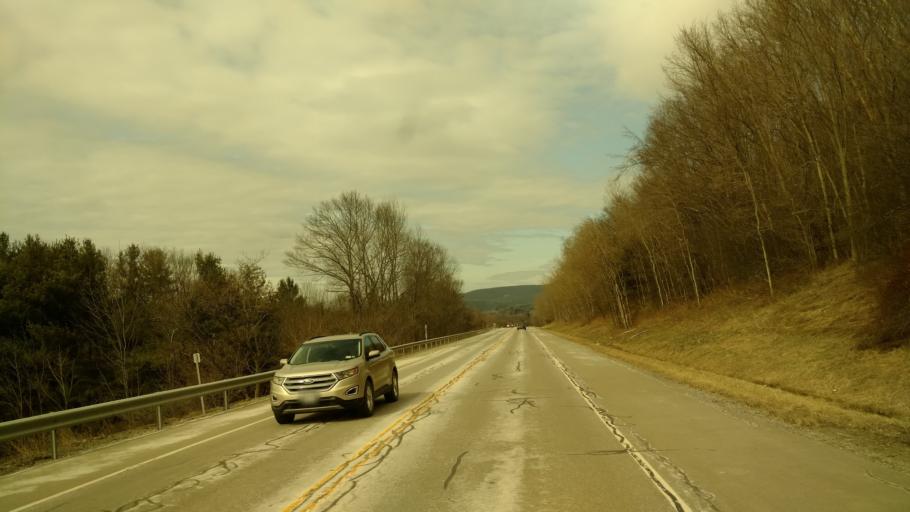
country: US
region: New York
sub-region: Allegany County
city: Wellsville
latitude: 42.0708
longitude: -77.9190
